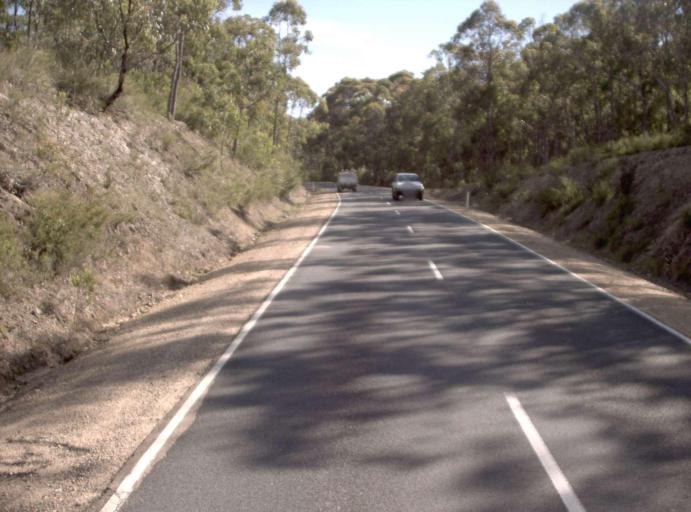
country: AU
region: Victoria
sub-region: East Gippsland
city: Lakes Entrance
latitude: -37.6470
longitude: 148.1069
